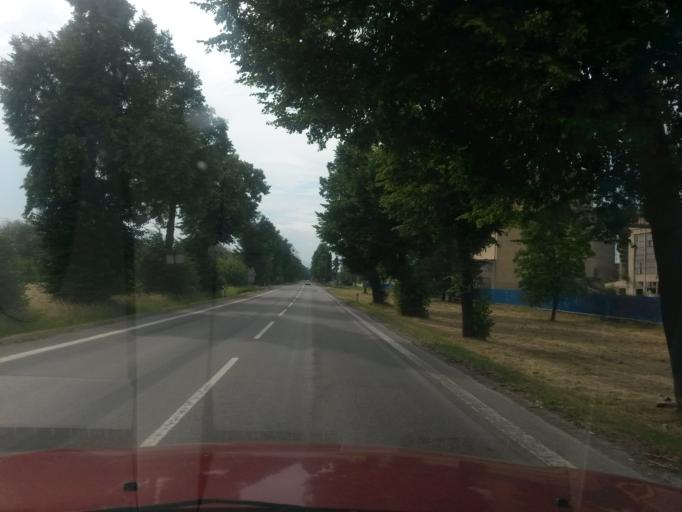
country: SK
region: Presovsky
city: Vranov nad Topl'ou
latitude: 48.8584
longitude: 21.7235
